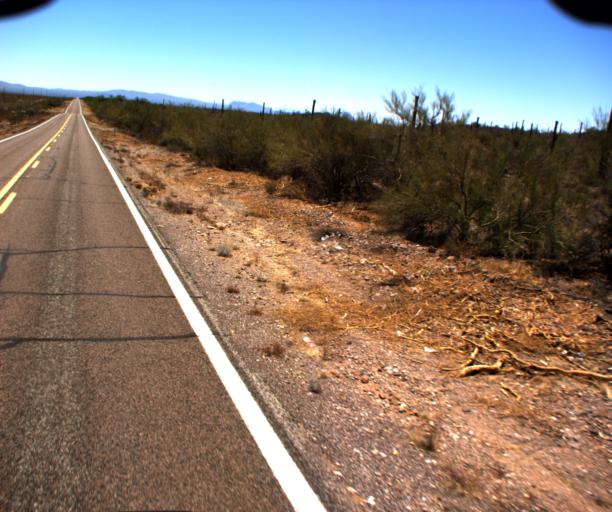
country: US
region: Arizona
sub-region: Pima County
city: Ajo
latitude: 32.2041
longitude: -112.5280
